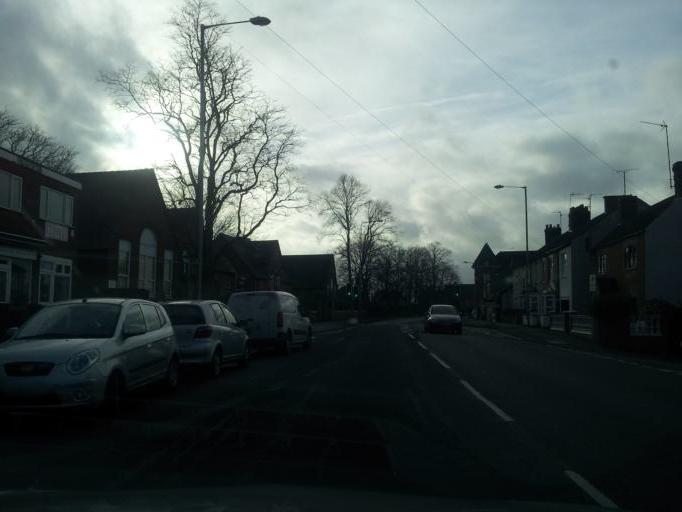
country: GB
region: England
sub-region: Northamptonshire
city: Finedon
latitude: 52.3390
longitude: -0.6503
